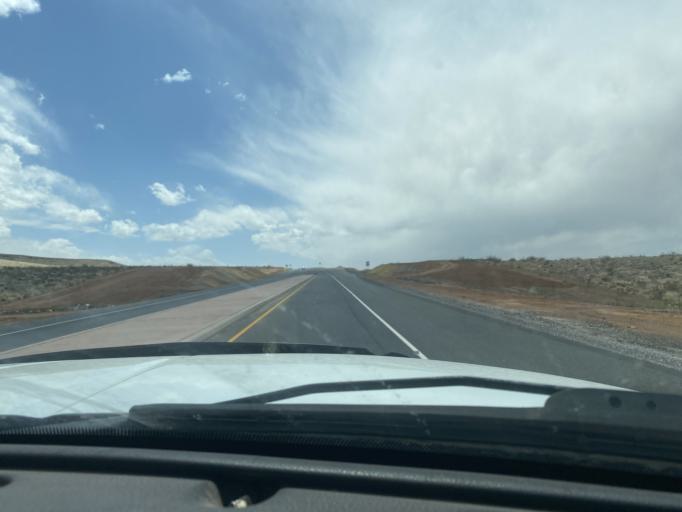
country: US
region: Utah
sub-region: Washington County
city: Hurricane
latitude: 37.1683
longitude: -113.3460
